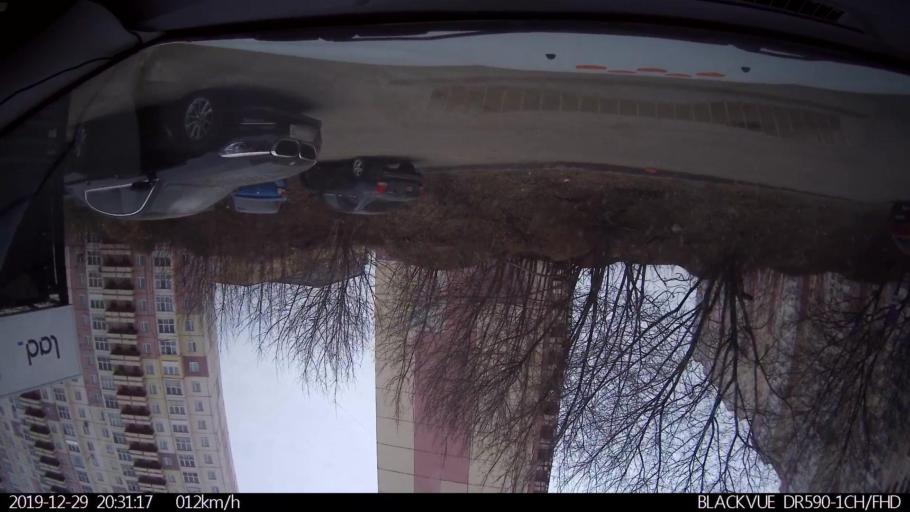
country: RU
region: Nizjnij Novgorod
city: Bor
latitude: 56.3163
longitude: 44.0603
